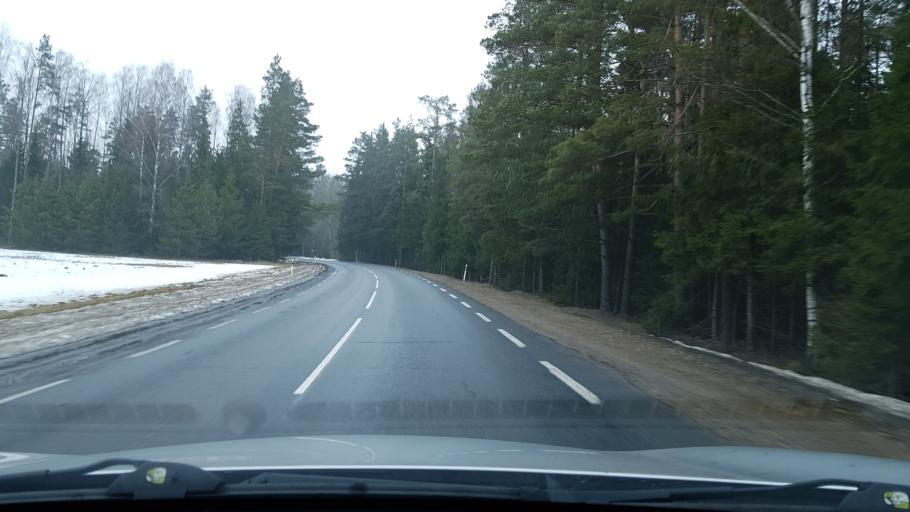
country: EE
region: Valgamaa
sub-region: Torva linn
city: Torva
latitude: 58.1699
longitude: 25.9643
